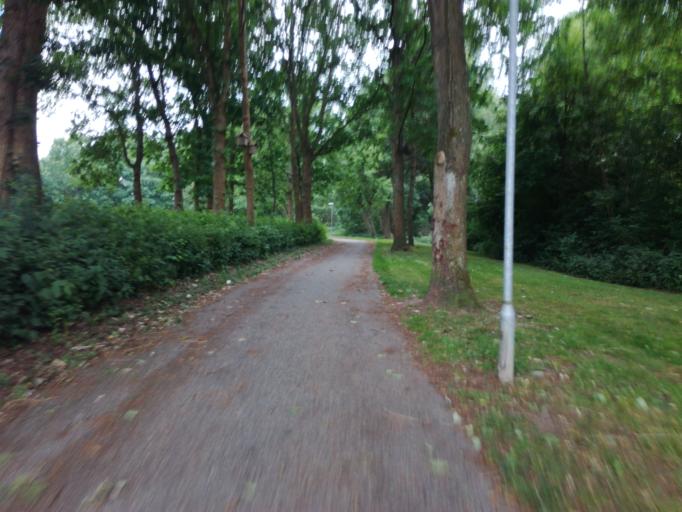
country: DK
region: South Denmark
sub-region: Vejle Kommune
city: Borkop
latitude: 55.6471
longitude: 9.6481
